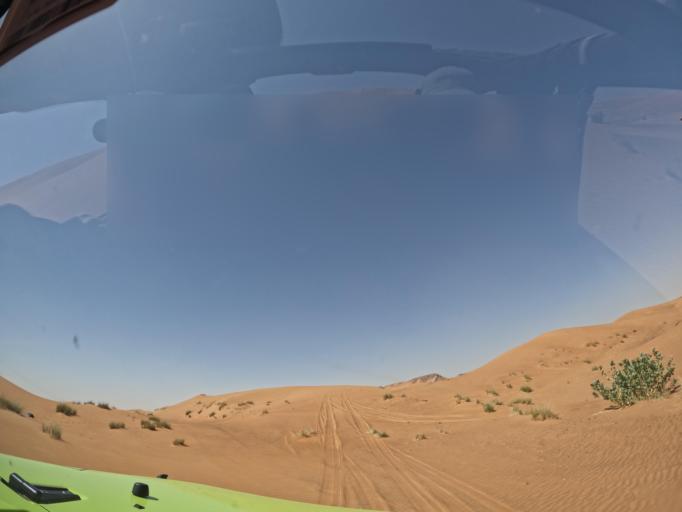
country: AE
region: Ash Shariqah
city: Adh Dhayd
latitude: 25.0190
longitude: 55.7463
